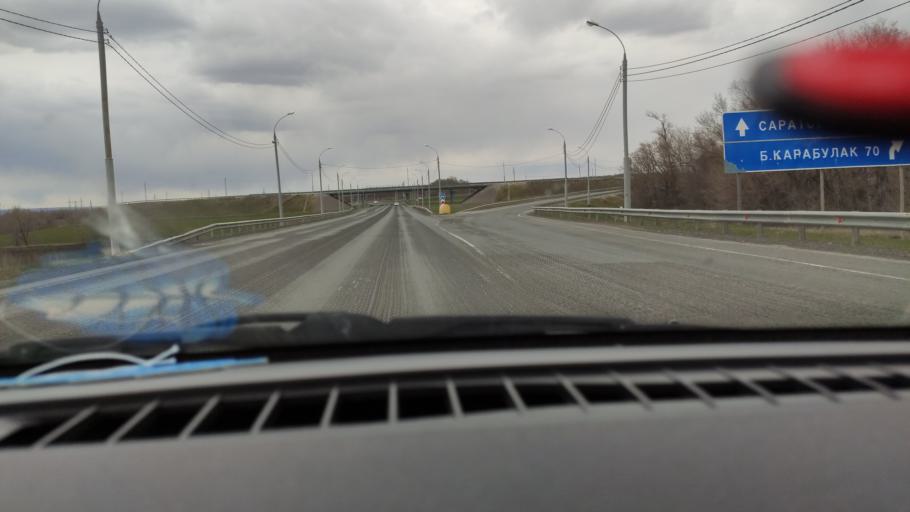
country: RU
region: Saratov
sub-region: Saratovskiy Rayon
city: Saratov
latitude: 51.7738
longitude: 46.0881
